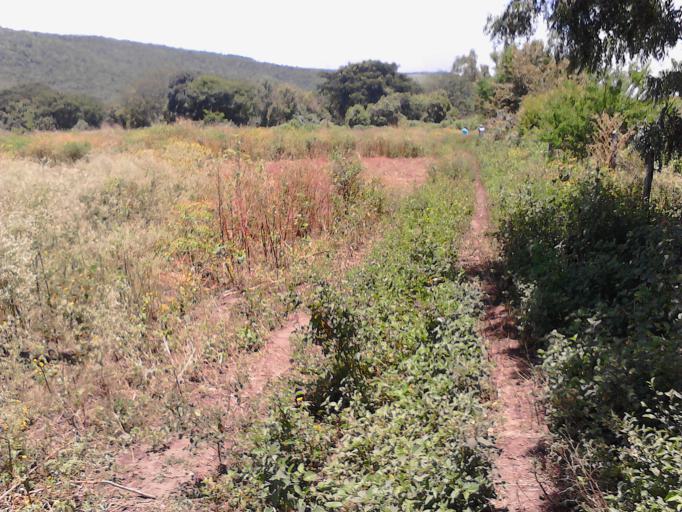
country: NI
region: Matagalpa
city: Ciudad Dario
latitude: 12.9158
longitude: -86.1348
